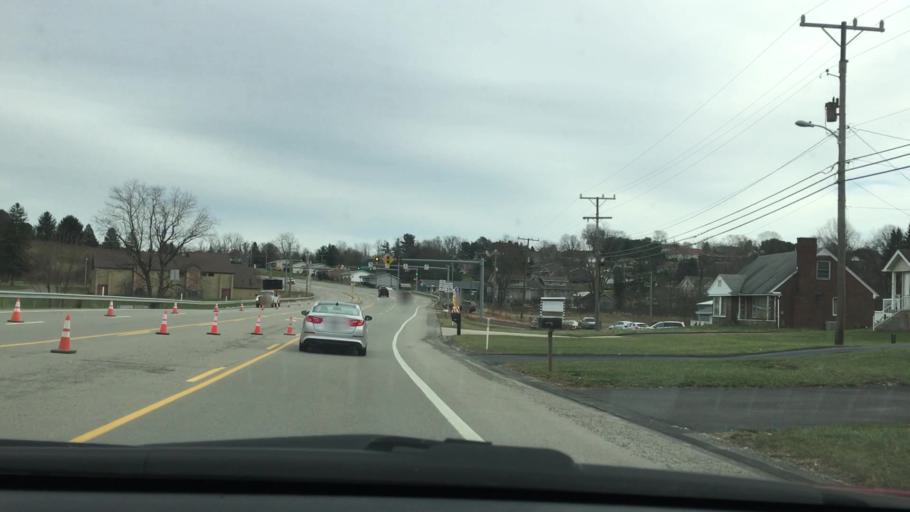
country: US
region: Pennsylvania
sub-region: Fayette County
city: South Uniontown
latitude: 39.8997
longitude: -79.7688
